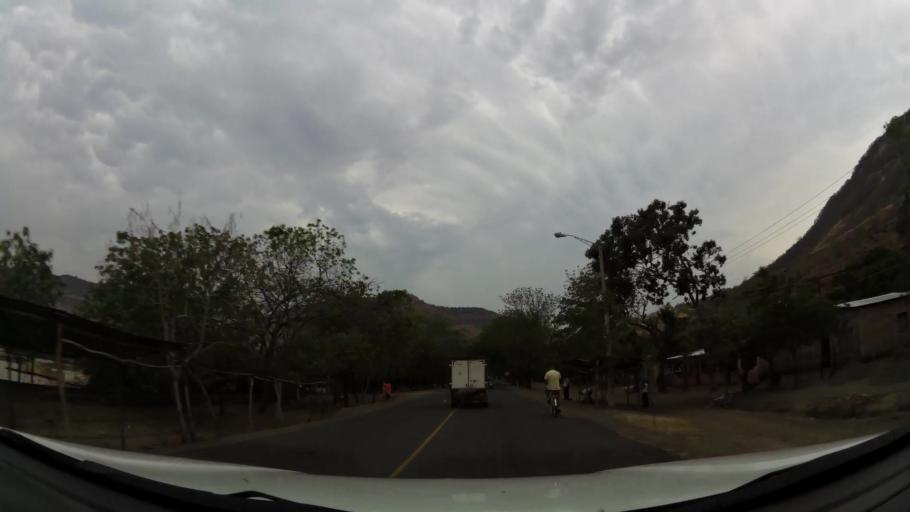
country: NI
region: Leon
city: Santa Rosa del Penon
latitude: 12.9369
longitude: -86.2046
